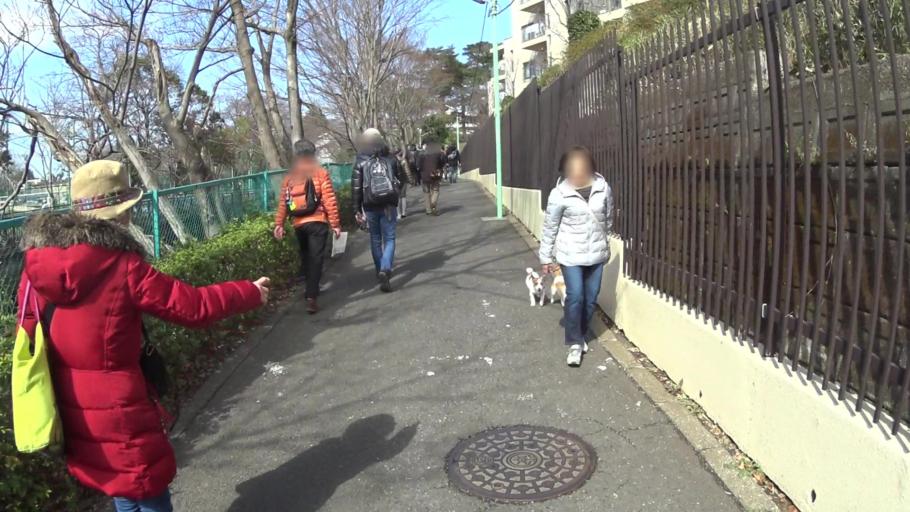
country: JP
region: Tokyo
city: Chofugaoka
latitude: 35.6426
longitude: 139.6009
